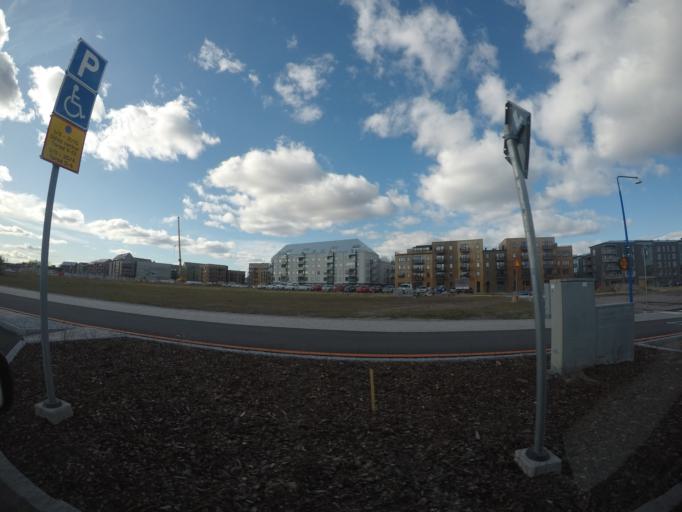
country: SE
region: OErebro
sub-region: Orebro Kommun
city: Orebro
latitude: 59.2527
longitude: 15.2061
